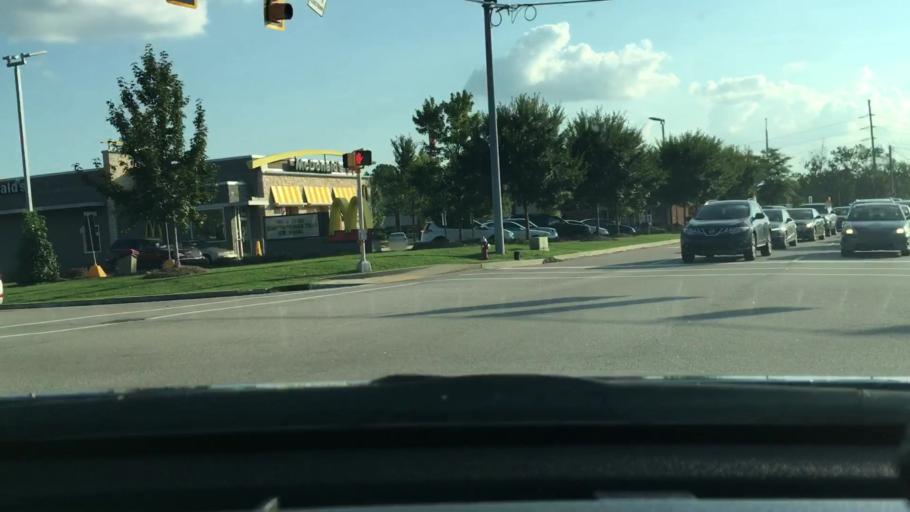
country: US
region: South Carolina
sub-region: Lexington County
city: Seven Oaks
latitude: 34.0745
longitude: -81.1554
